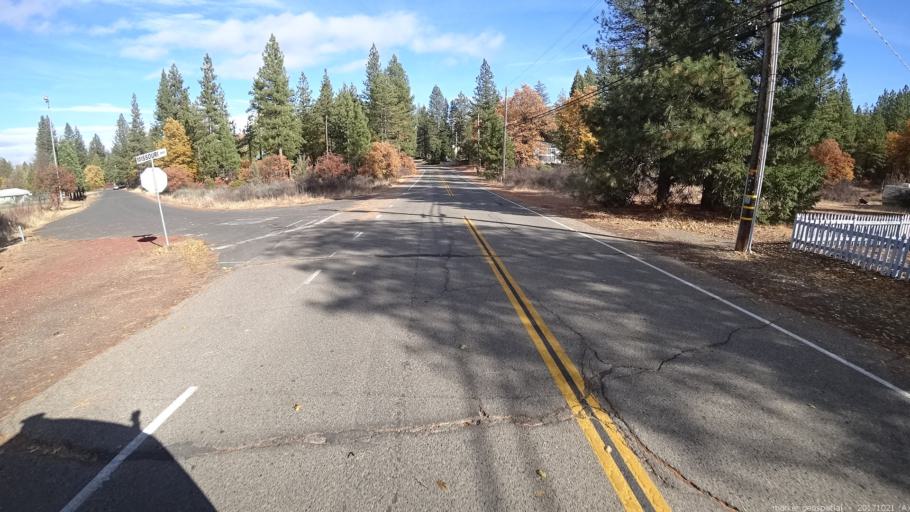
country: US
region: California
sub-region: Shasta County
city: Burney
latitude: 40.8762
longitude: -121.6644
